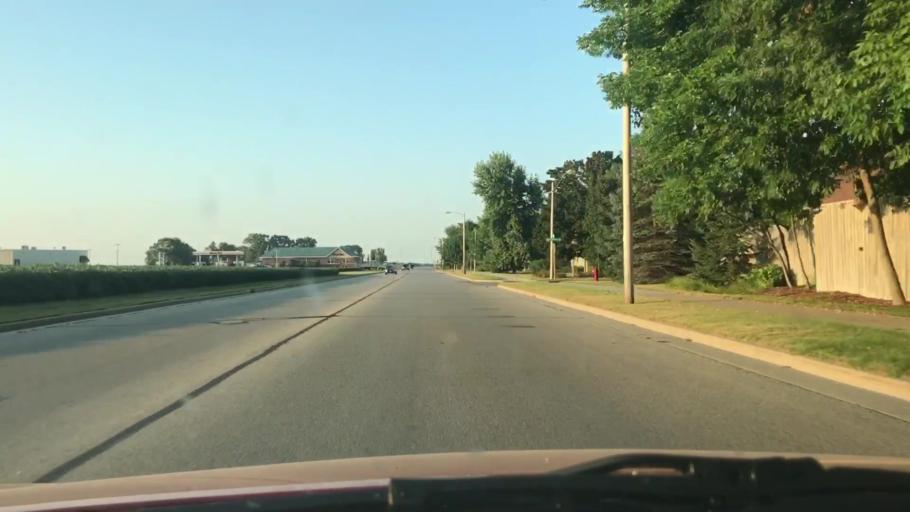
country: US
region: Wisconsin
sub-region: Outagamie County
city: Seymour
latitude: 44.5042
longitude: -88.3205
